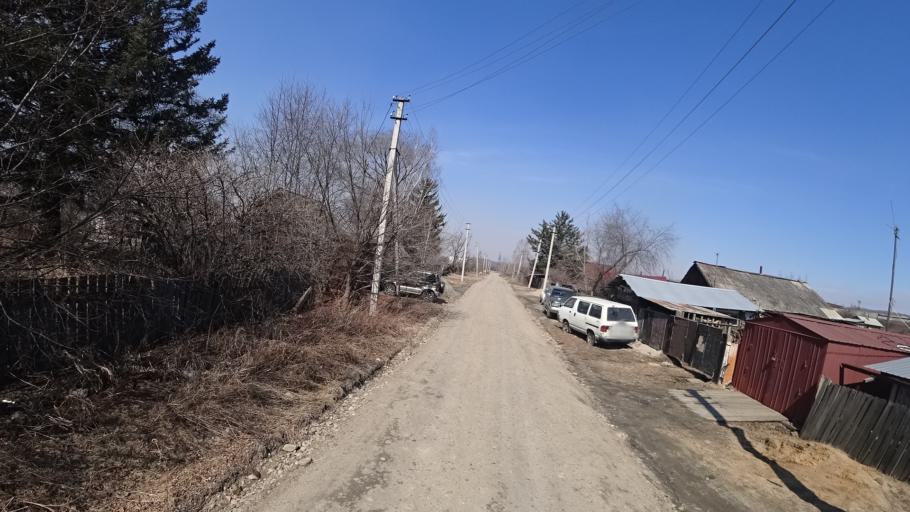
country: RU
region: Amur
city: Novobureyskiy
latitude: 49.7889
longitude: 129.8541
